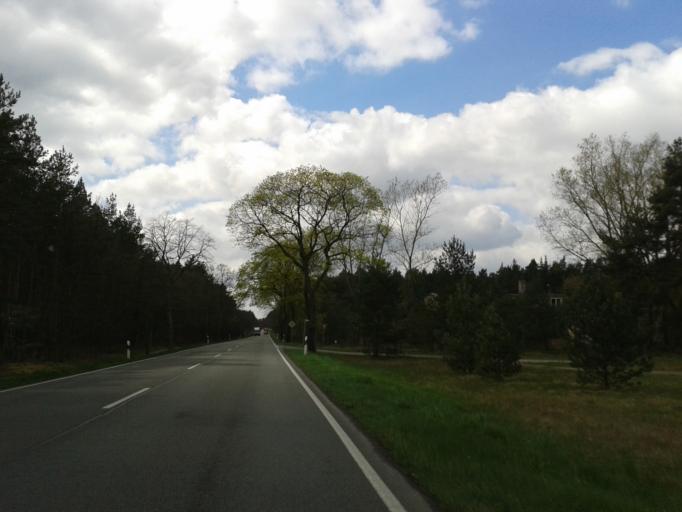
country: DE
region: Lower Saxony
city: Bergen an der Dumme
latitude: 52.8823
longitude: 11.0179
